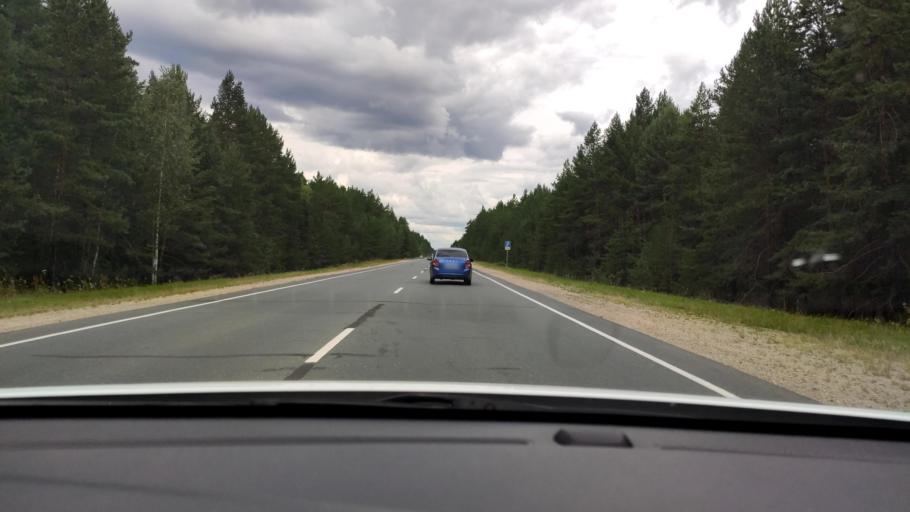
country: RU
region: Mariy-El
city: Krasnogorskiy
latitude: 56.0664
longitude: 48.3662
